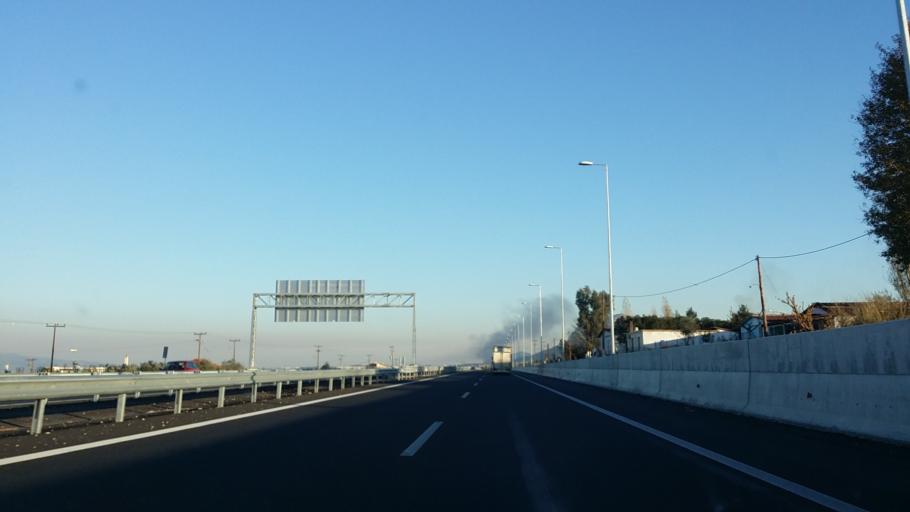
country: GR
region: Peloponnese
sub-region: Nomos Korinthias
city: Zevgolateio
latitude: 37.9253
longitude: 22.7985
